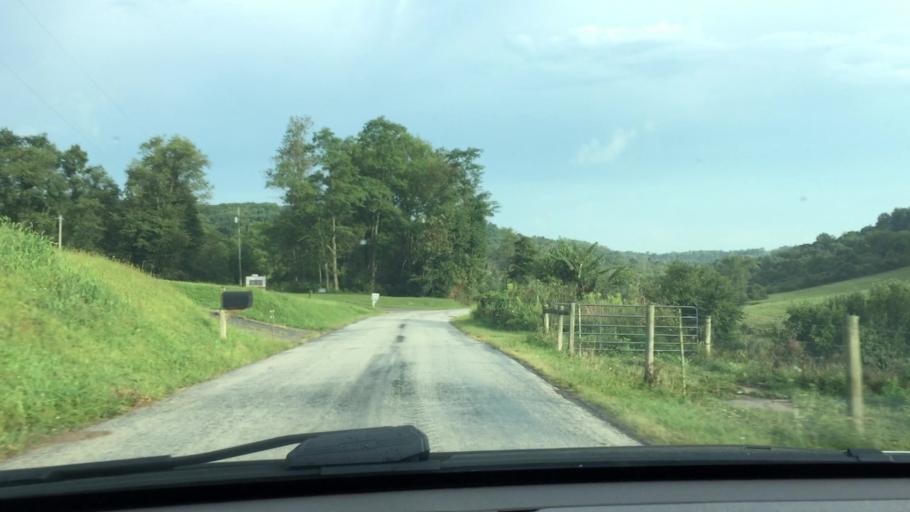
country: US
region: Pennsylvania
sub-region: Washington County
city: McGovern
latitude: 40.1994
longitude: -80.1762
